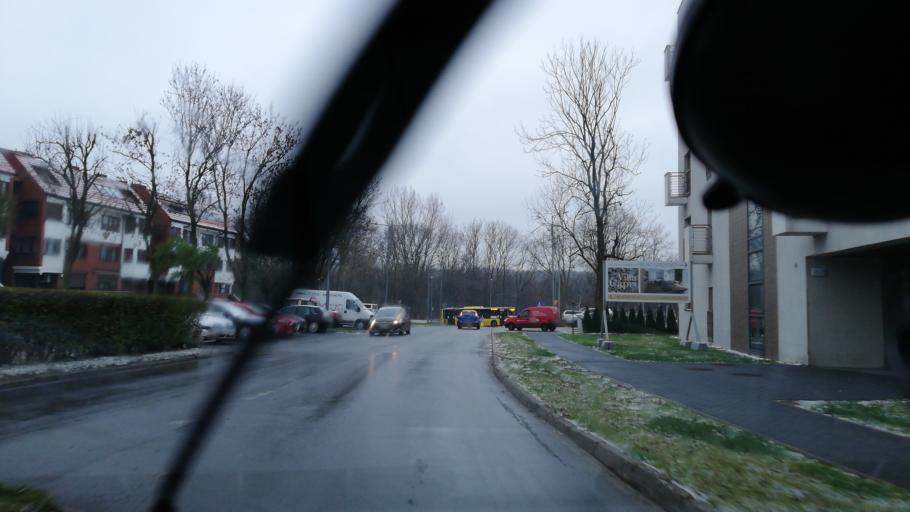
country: PL
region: Silesian Voivodeship
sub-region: Chorzow
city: Chorzow
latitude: 50.2984
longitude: 18.9970
